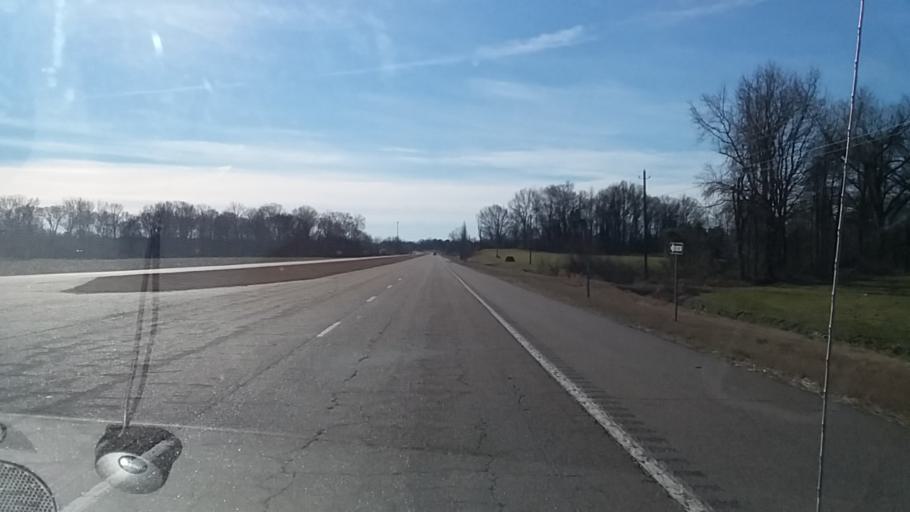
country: US
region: Tennessee
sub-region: Lauderdale County
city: Halls
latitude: 35.9279
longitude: -89.2840
